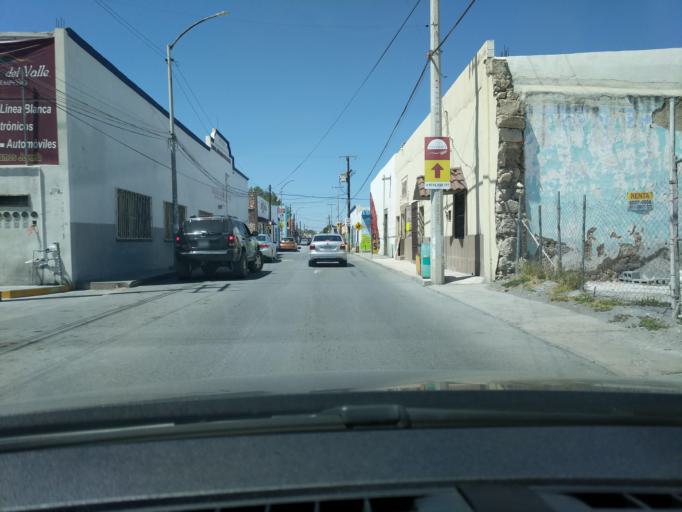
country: MX
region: Nuevo Leon
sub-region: Salinas Victoria
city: Las Torres
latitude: 25.9608
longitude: -100.2912
